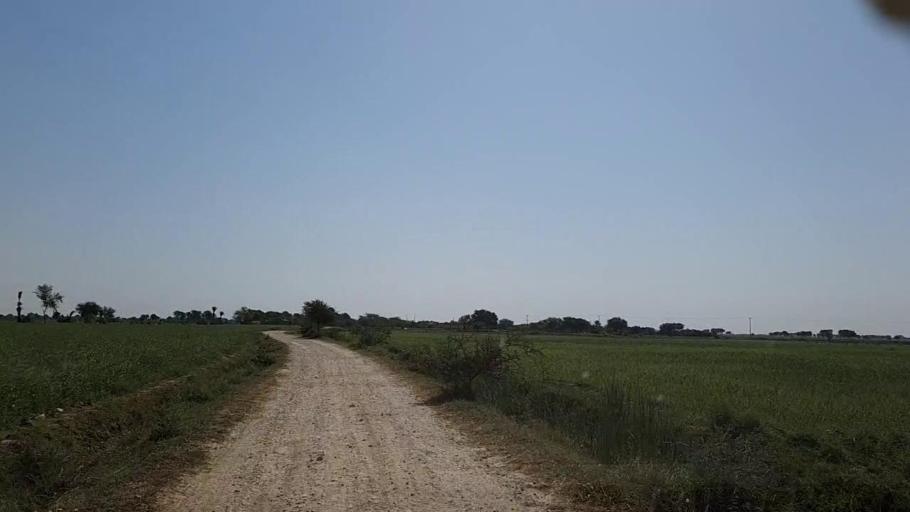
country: PK
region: Sindh
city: Mirpur Batoro
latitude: 24.6816
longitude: 68.2923
